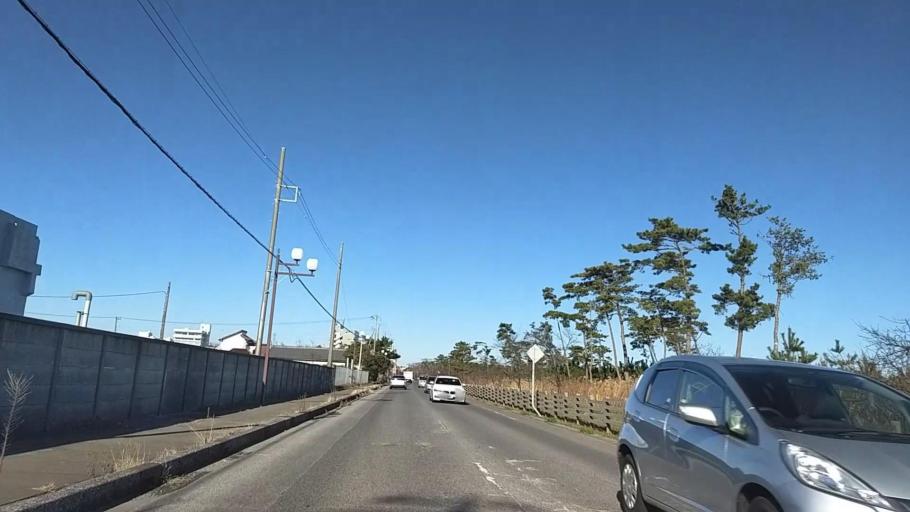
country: JP
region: Chiba
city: Mobara
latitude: 35.4245
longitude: 140.3942
